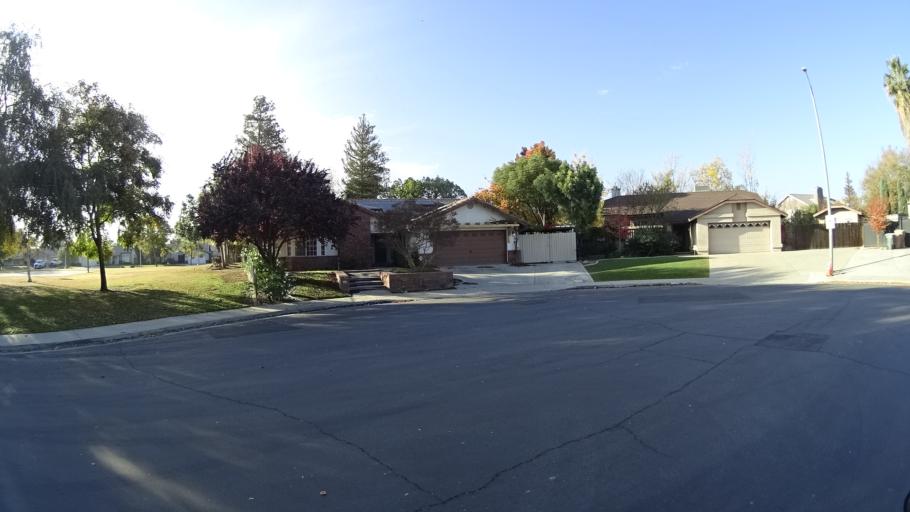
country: US
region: California
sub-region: Kern County
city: Rosedale
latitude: 35.3522
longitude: -119.1587
